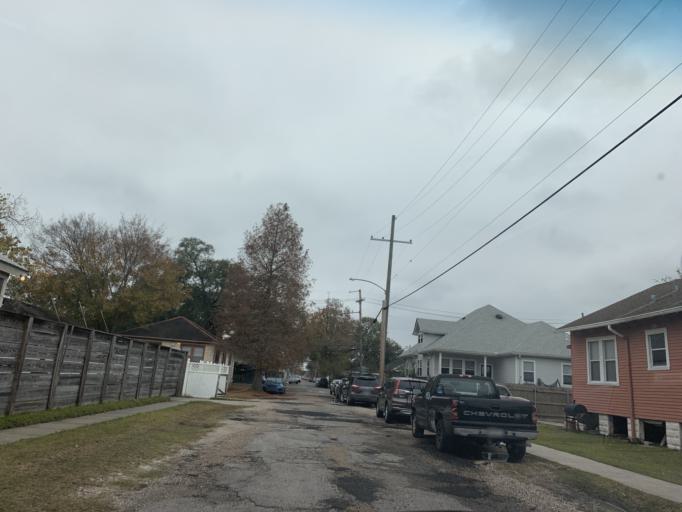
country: US
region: Louisiana
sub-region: Jefferson Parish
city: Metairie
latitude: 29.9904
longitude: -90.1081
